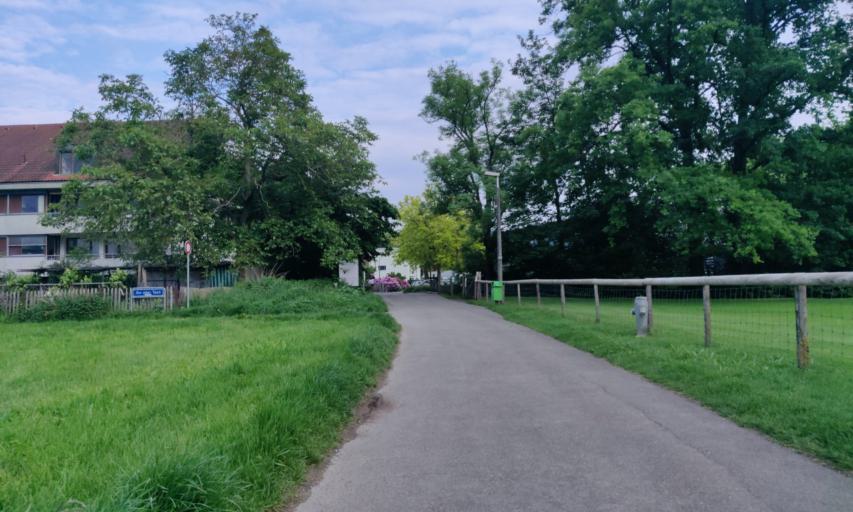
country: CH
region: Basel-City
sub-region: Basel-Stadt
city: Riehen
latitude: 47.5820
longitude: 7.6381
